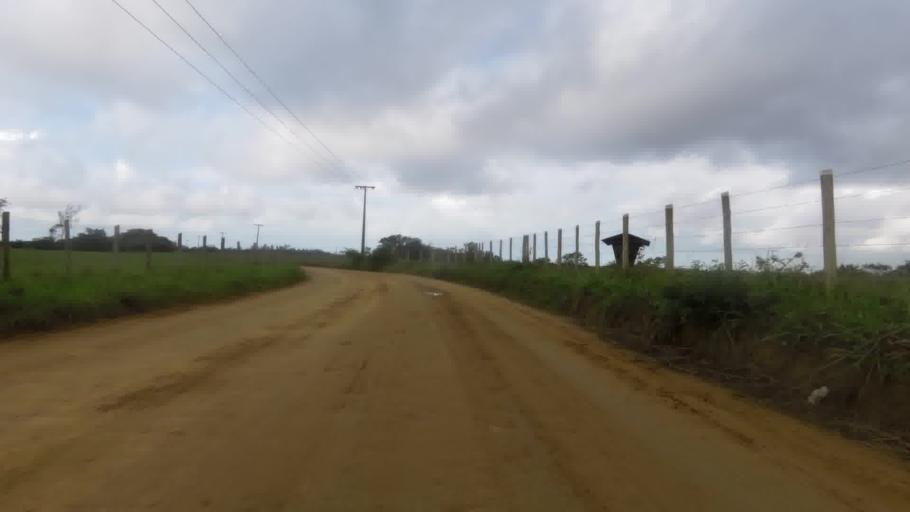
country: BR
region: Espirito Santo
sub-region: Piuma
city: Piuma
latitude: -20.7738
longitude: -40.6306
